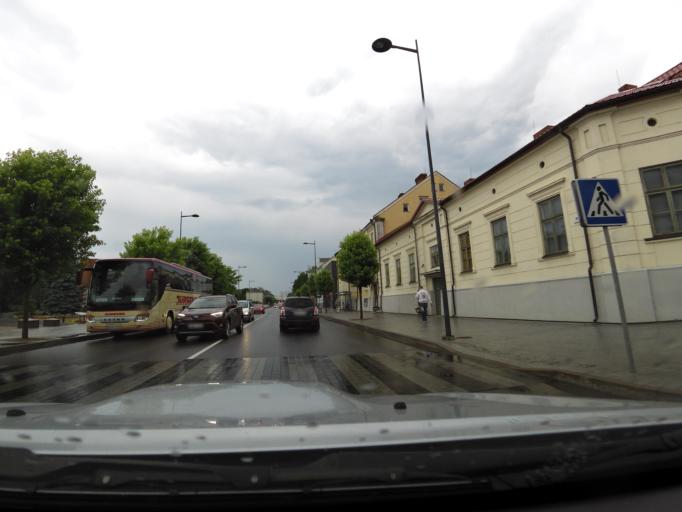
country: LT
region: Marijampoles apskritis
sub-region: Marijampole Municipality
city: Marijampole
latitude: 54.5518
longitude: 23.3484
